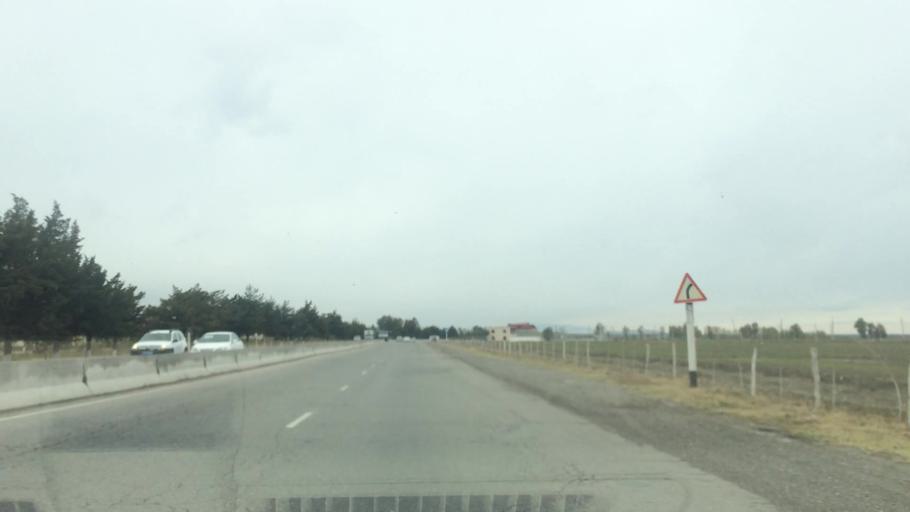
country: UZ
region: Samarqand
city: Bulung'ur
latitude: 39.7608
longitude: 67.2524
